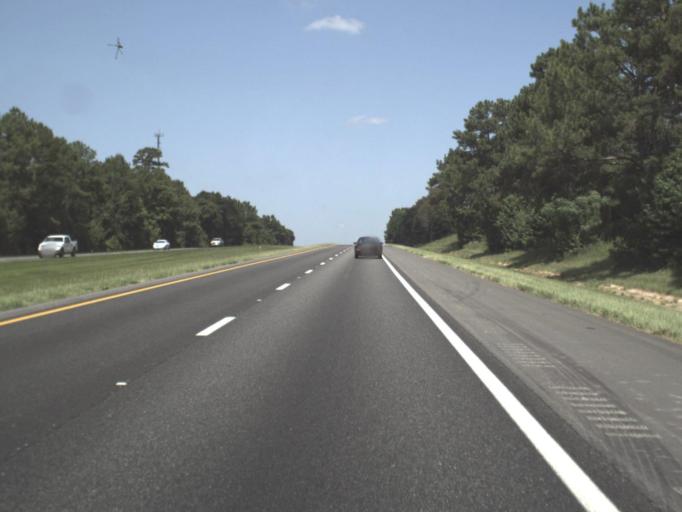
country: US
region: Florida
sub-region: Madison County
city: Madison
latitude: 30.4354
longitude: -83.4885
